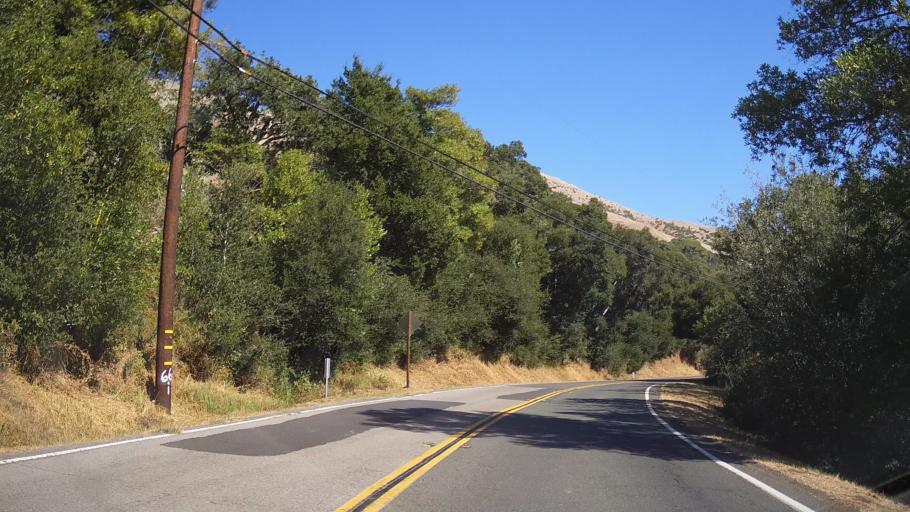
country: US
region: California
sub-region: Marin County
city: Inverness
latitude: 38.0783
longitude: -122.7765
